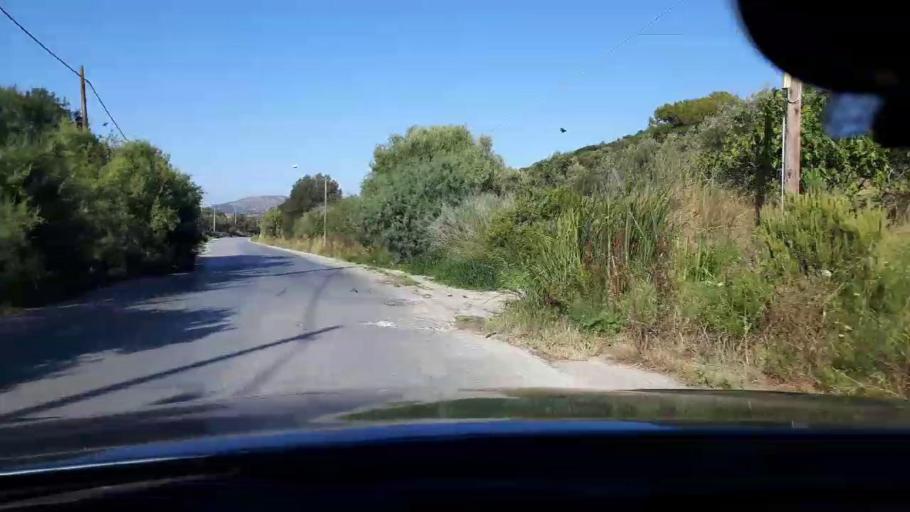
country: GR
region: Attica
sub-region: Nomarchia Anatolikis Attikis
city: Markopoulo
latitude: 37.8845
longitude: 23.9483
